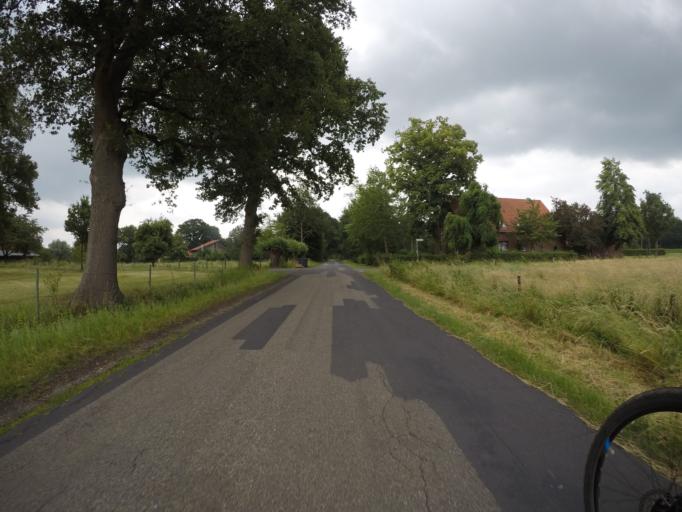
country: DE
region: North Rhine-Westphalia
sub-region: Regierungsbezirk Dusseldorf
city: Hunxe
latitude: 51.6421
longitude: 6.7846
